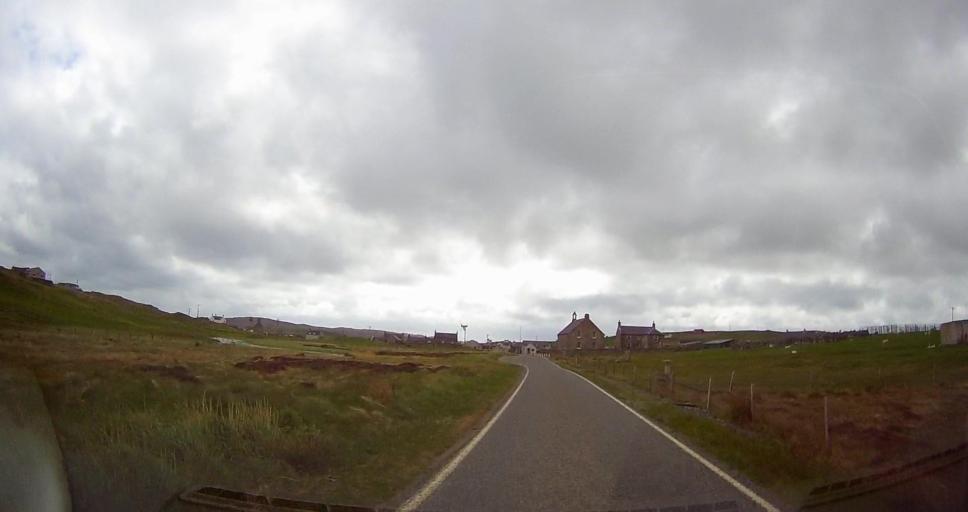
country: GB
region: Scotland
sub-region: Shetland Islands
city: Sandwick
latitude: 60.2317
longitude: -1.5588
